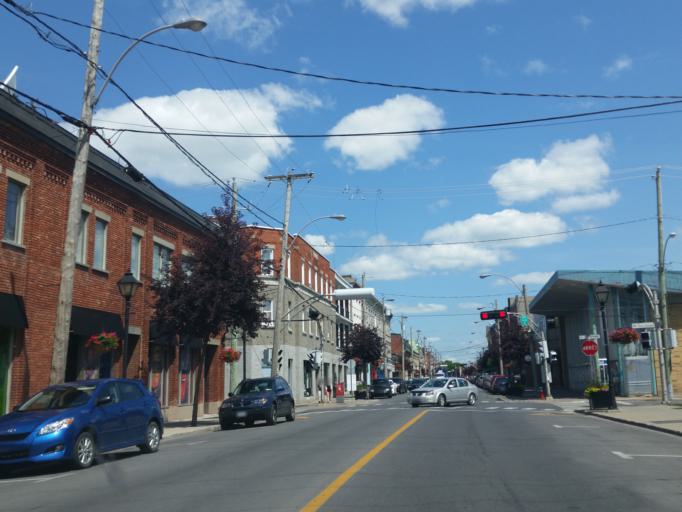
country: CA
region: Quebec
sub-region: Monteregie
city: Saint-Jean-sur-Richelieu
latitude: 45.3042
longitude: -73.2508
